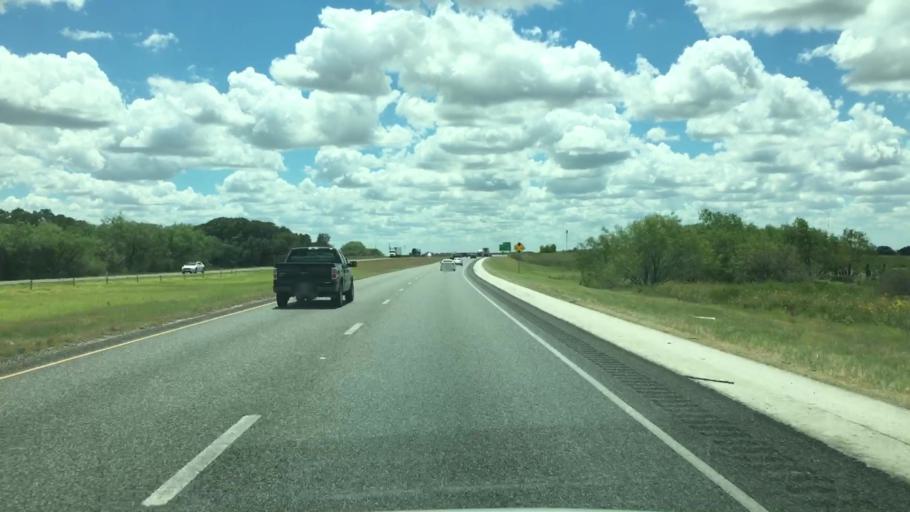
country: US
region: Texas
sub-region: Bexar County
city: Elmendorf
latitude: 29.1488
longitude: -98.4283
